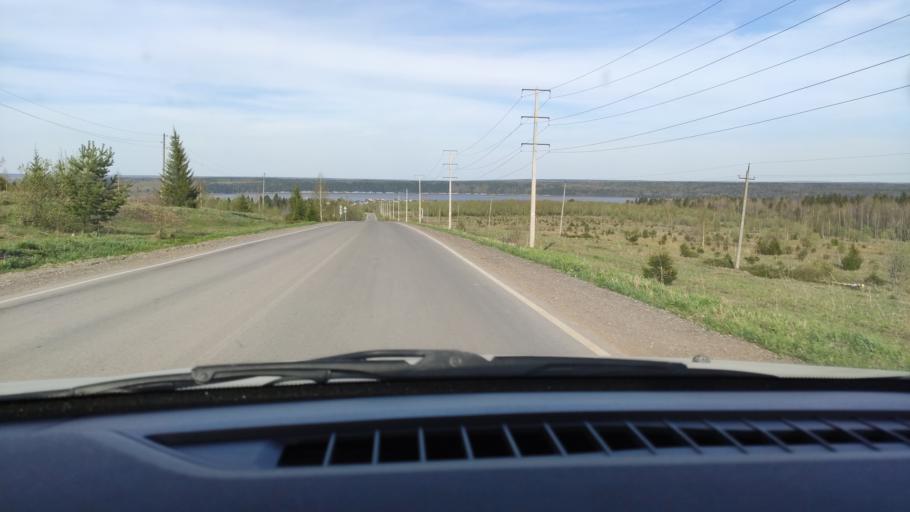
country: RU
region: Perm
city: Novyye Lyady
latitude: 57.9209
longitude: 56.6713
